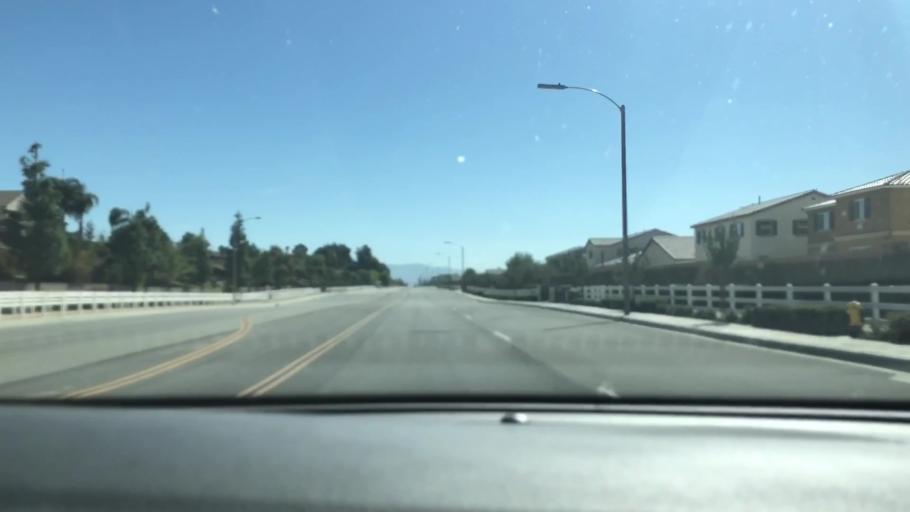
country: US
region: California
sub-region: Riverside County
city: Wildomar
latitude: 33.5952
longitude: -117.2605
